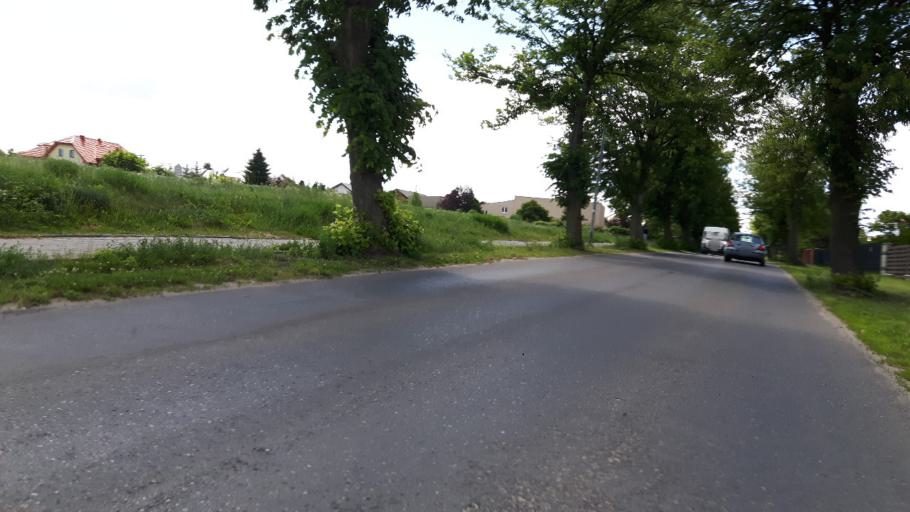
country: PL
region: Pomeranian Voivodeship
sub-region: Powiat pucki
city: Mosty
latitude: 54.6015
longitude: 18.4981
